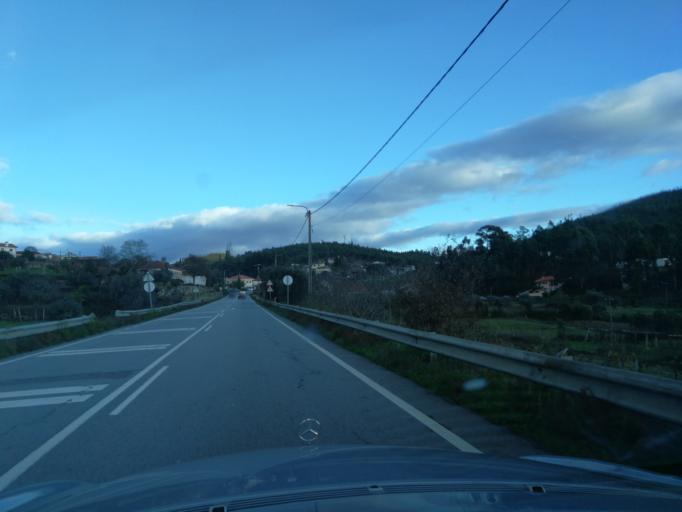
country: PT
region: Braga
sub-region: Barcelos
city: Vila Frescainha
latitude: 41.5722
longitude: -8.6912
